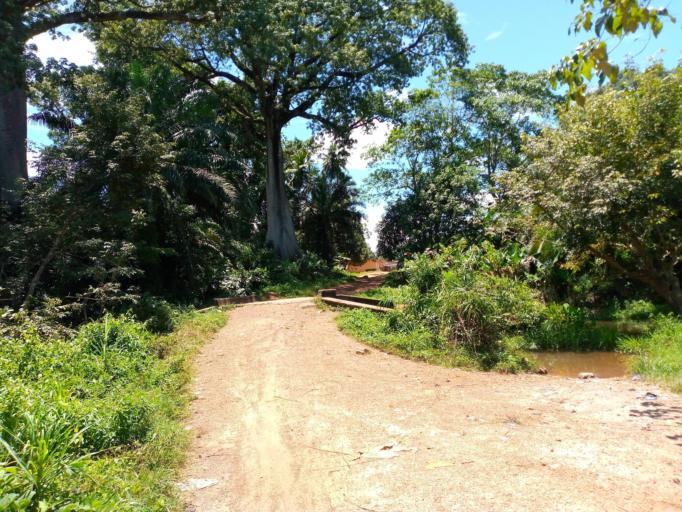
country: SL
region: Northern Province
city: Makeni
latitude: 9.0350
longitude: -12.1593
